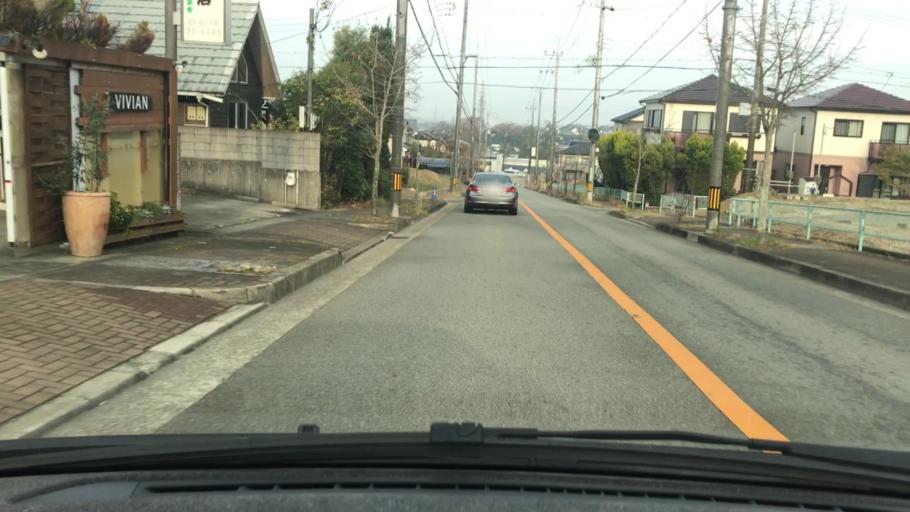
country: JP
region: Hyogo
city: Sandacho
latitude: 34.8255
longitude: 135.2514
